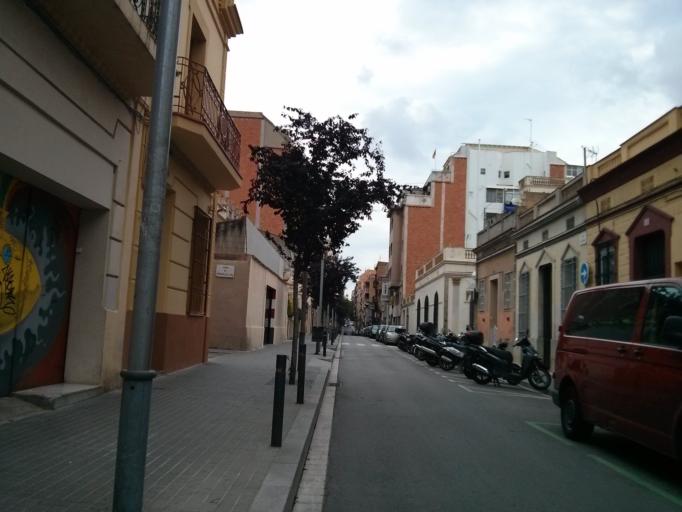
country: ES
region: Catalonia
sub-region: Provincia de Barcelona
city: Gracia
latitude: 41.4054
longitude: 2.1583
